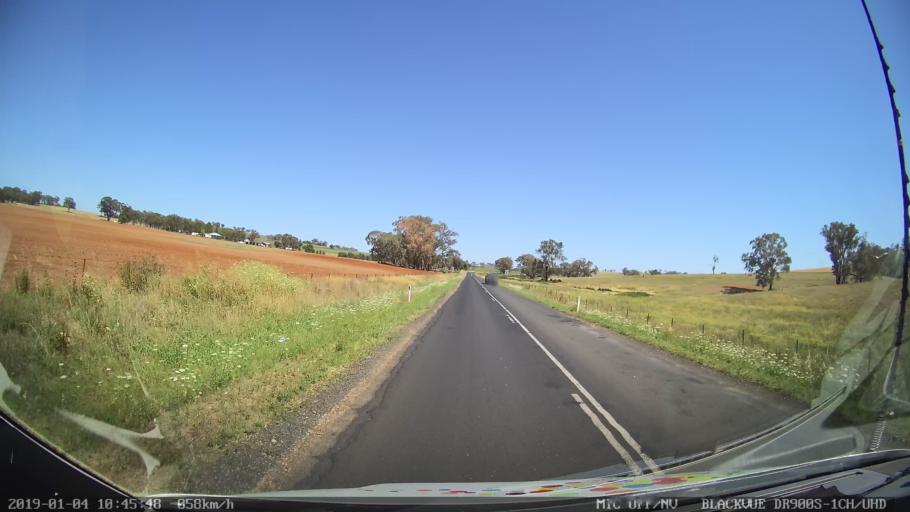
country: AU
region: New South Wales
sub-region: Cabonne
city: Molong
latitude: -33.2865
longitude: 148.7279
